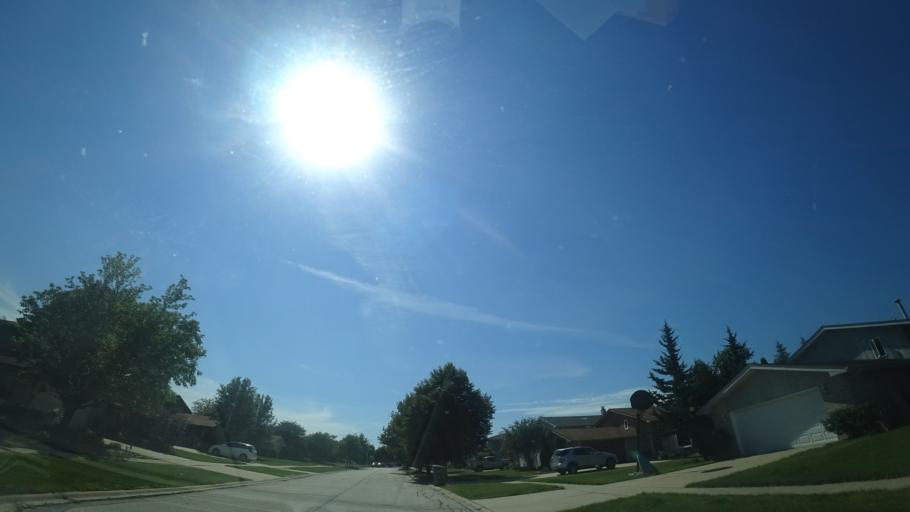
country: US
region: Illinois
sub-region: Will County
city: Mokena
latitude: 41.5720
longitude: -87.8991
